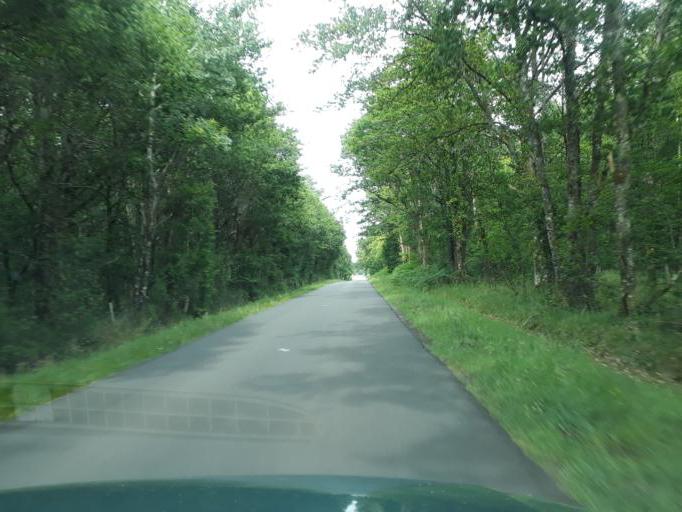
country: FR
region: Centre
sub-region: Departement du Loiret
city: Menestreau-en-Villette
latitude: 47.7189
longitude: 2.0114
